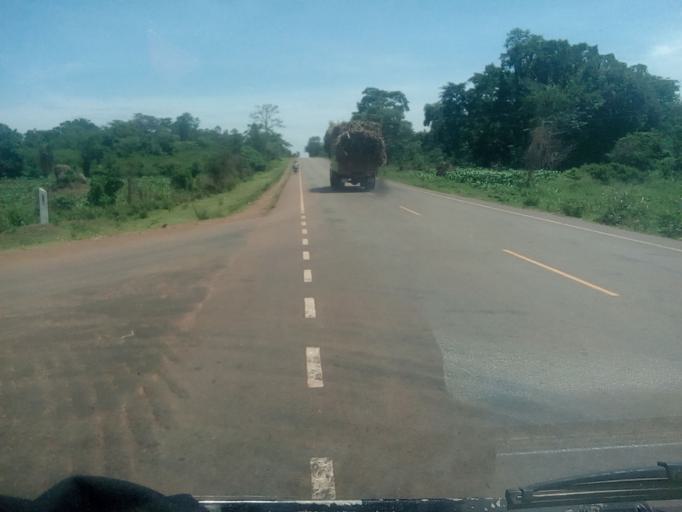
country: UG
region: Eastern Region
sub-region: Kamuli District
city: Kamuli
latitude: 0.9286
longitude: 33.1144
